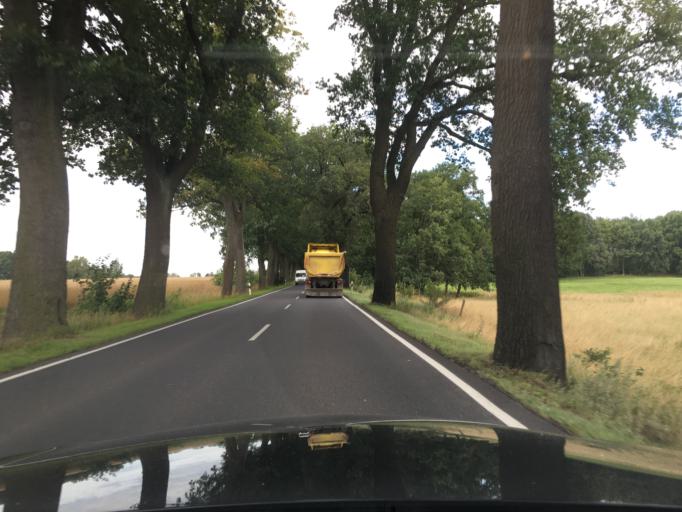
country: DE
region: Brandenburg
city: Gransee
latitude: 52.9195
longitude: 13.1572
